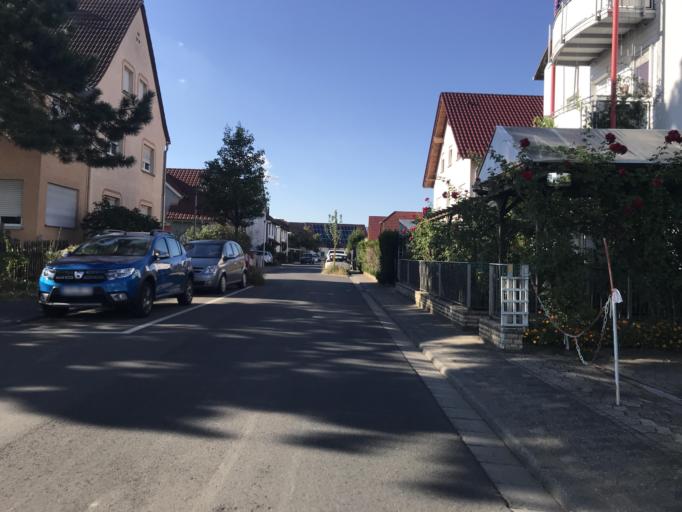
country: DE
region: Rheinland-Pfalz
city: Gau-Algesheim
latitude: 49.9753
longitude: 8.0097
